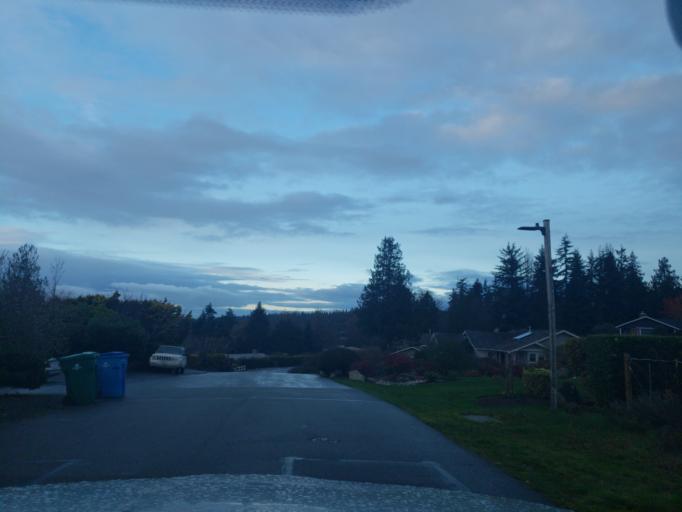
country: US
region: Washington
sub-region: King County
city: Shoreline
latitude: 47.7553
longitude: -122.3742
